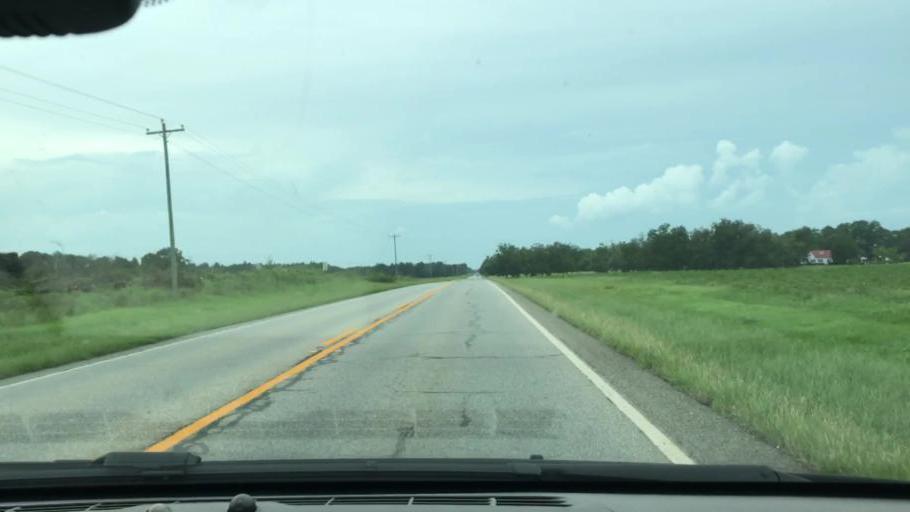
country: US
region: Georgia
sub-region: Early County
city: Blakely
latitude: 31.3549
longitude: -84.9725
